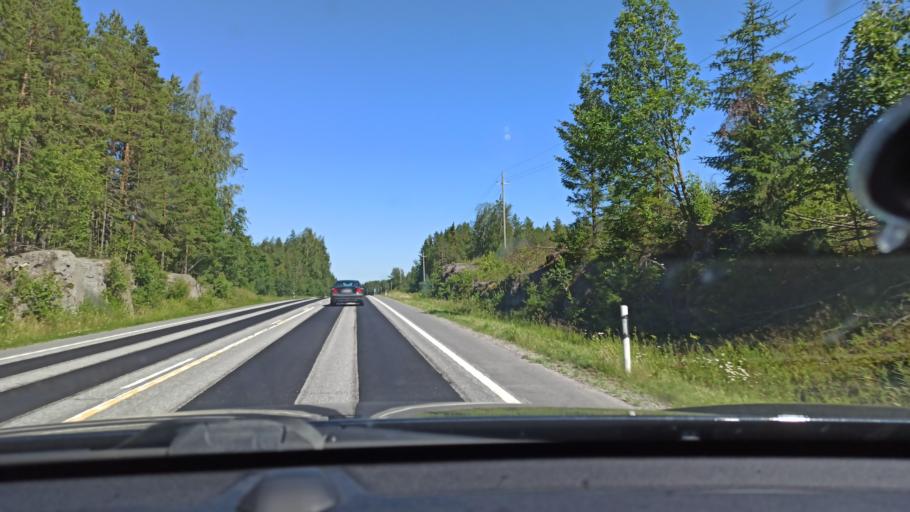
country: FI
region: Ostrobothnia
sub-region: Vaasa
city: Voera
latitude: 63.2036
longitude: 22.1252
